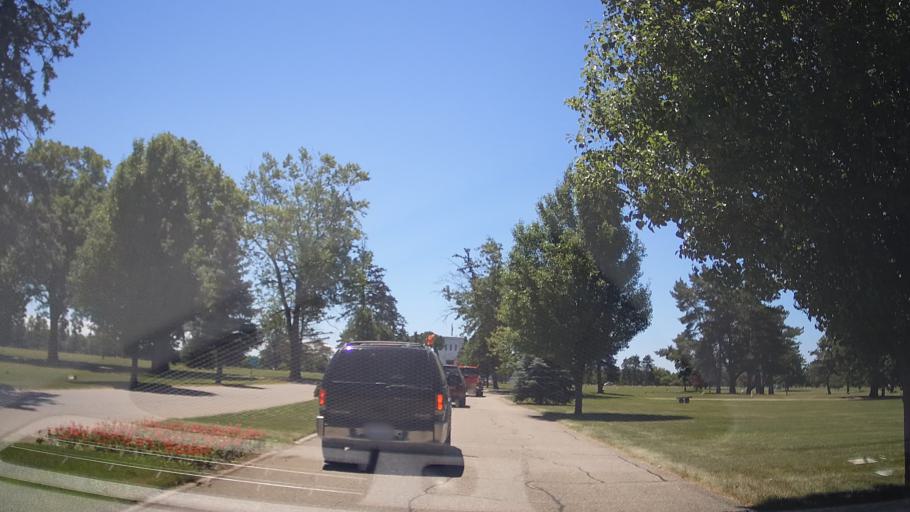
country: US
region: Michigan
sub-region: Oakland County
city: Troy
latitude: 42.5882
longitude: -83.1637
